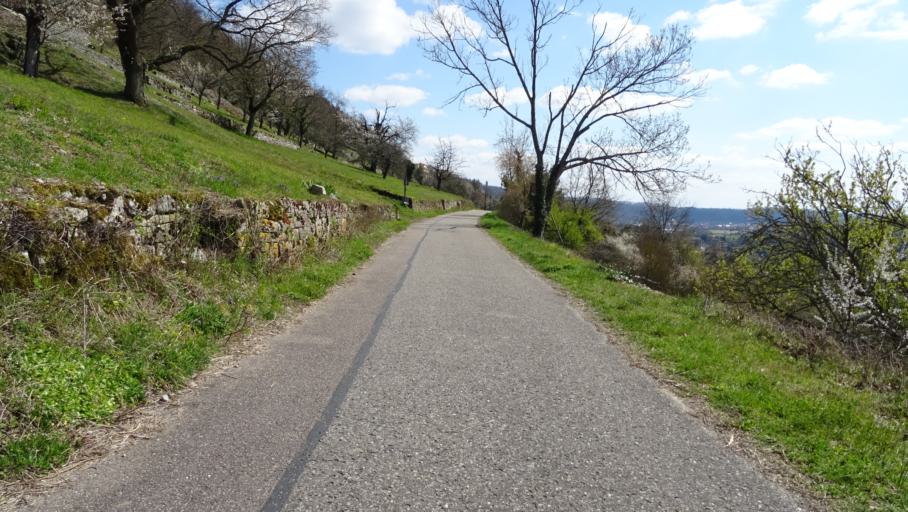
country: DE
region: Baden-Wuerttemberg
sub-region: Karlsruhe Region
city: Neckarzimmern
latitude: 49.3254
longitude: 9.1215
